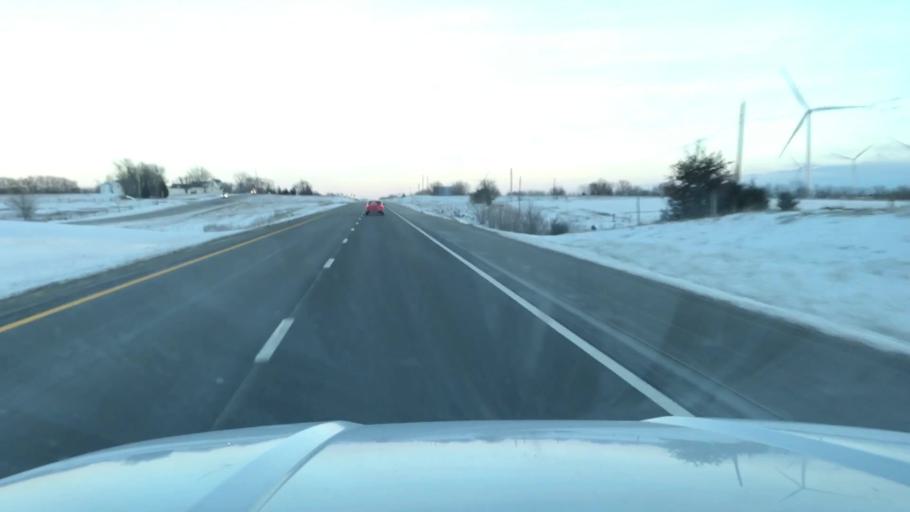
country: US
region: Missouri
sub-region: DeKalb County
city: Maysville
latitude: 39.7616
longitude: -94.4157
